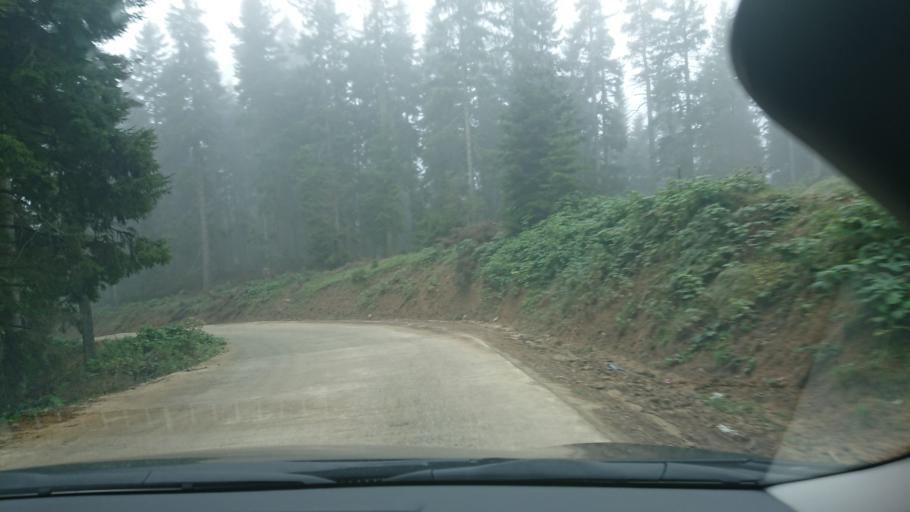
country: TR
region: Gumushane
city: Kurtun
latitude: 40.6651
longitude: 39.0127
